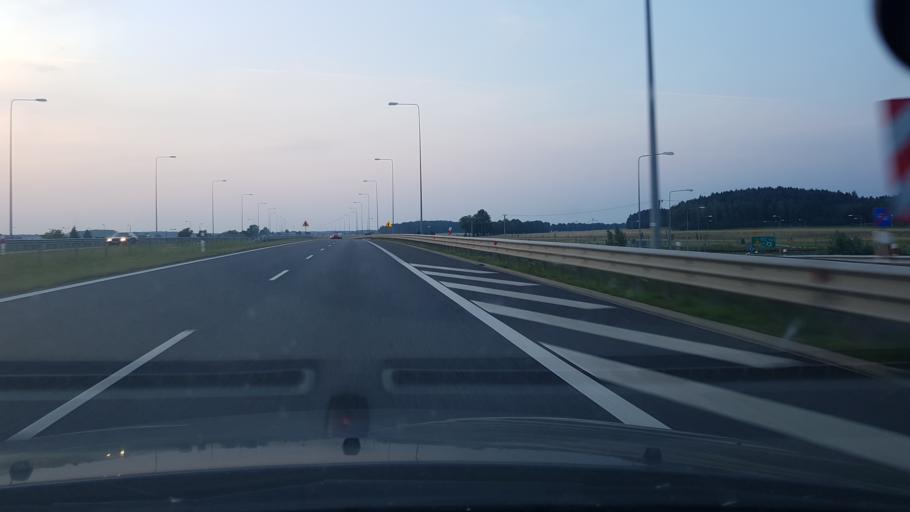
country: PL
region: Warmian-Masurian Voivodeship
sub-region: Powiat nidzicki
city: Nidzica
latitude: 53.4102
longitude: 20.3392
